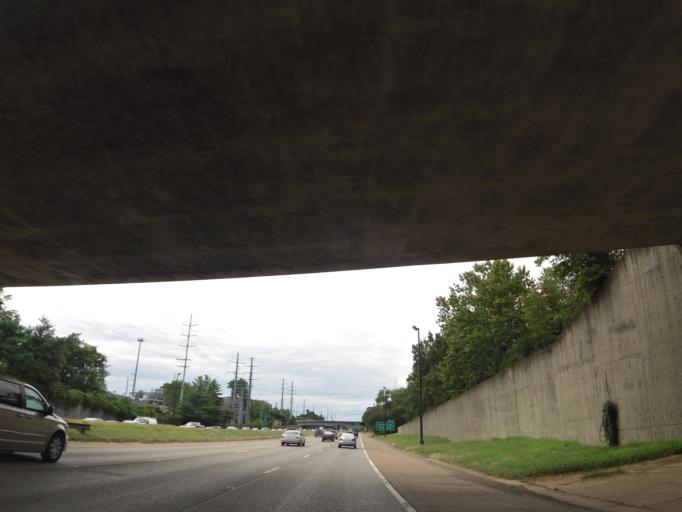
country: US
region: Tennessee
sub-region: Davidson County
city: Oak Hill
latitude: 36.1261
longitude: -86.8142
